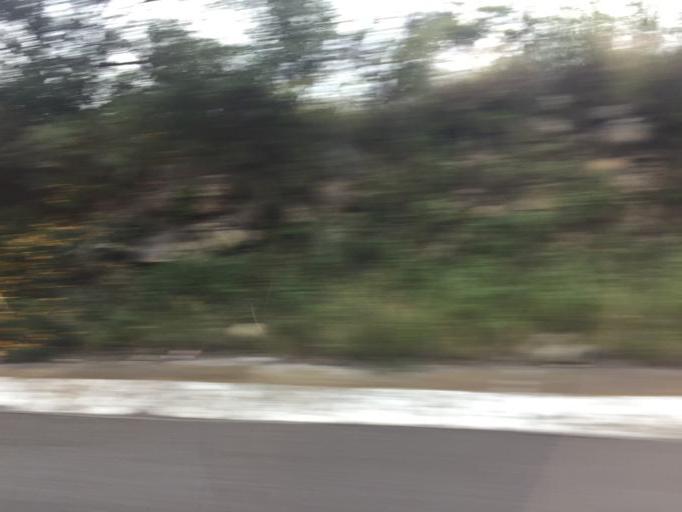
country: MX
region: Michoacan
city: Panindicuaro de la Reforma
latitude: 19.9716
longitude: -101.7219
